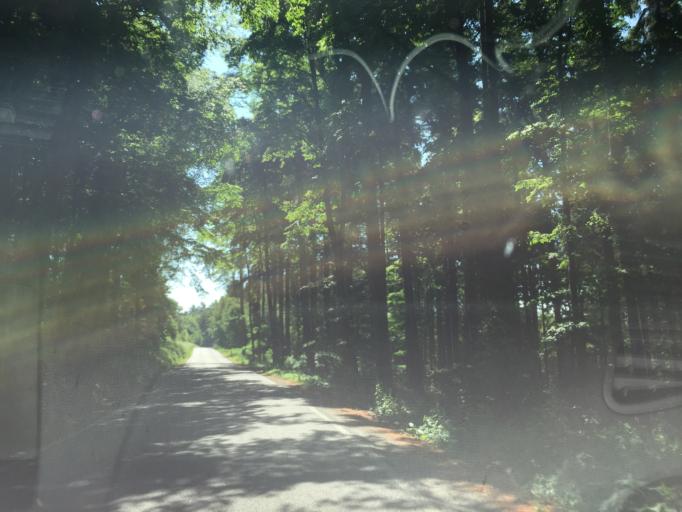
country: DE
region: Baden-Wuerttemberg
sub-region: Karlsruhe Region
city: Walldurn
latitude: 49.6145
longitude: 9.3329
